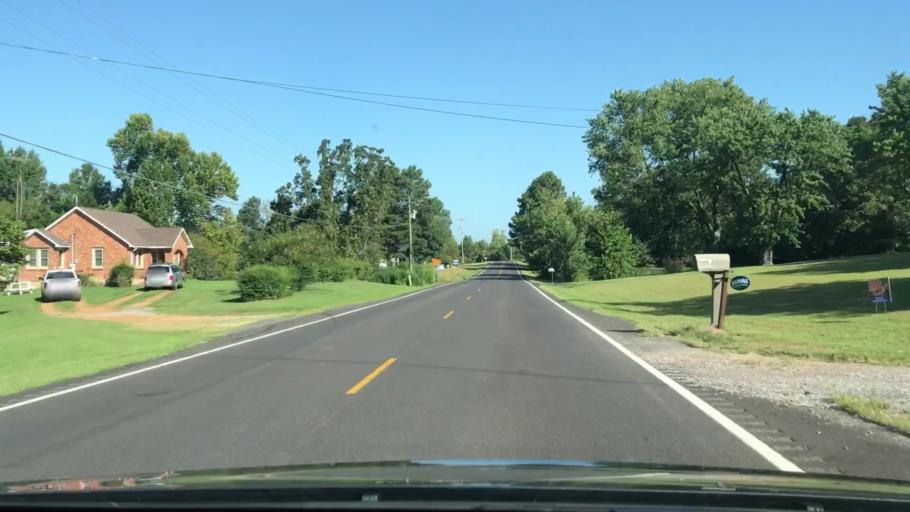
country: US
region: Kentucky
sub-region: Marshall County
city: Benton
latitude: 36.7726
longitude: -88.4411
